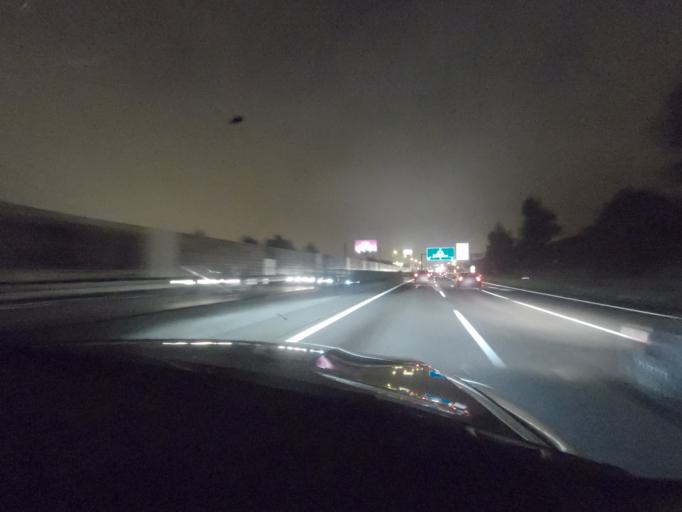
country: PT
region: Lisbon
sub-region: Loures
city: Santa Iria da Azoia
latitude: 38.8549
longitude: -9.0845
